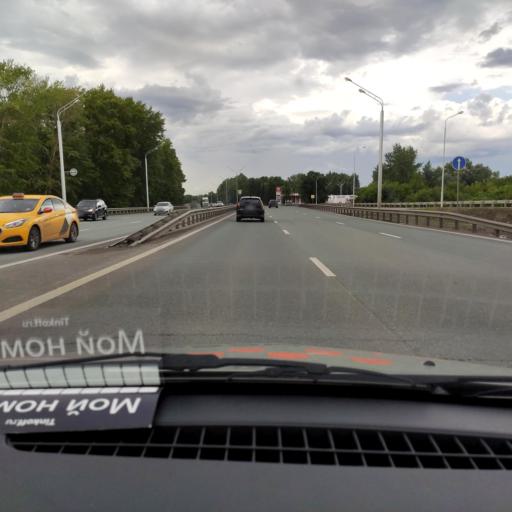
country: RU
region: Bashkortostan
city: Ufa
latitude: 54.6200
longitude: 55.9247
